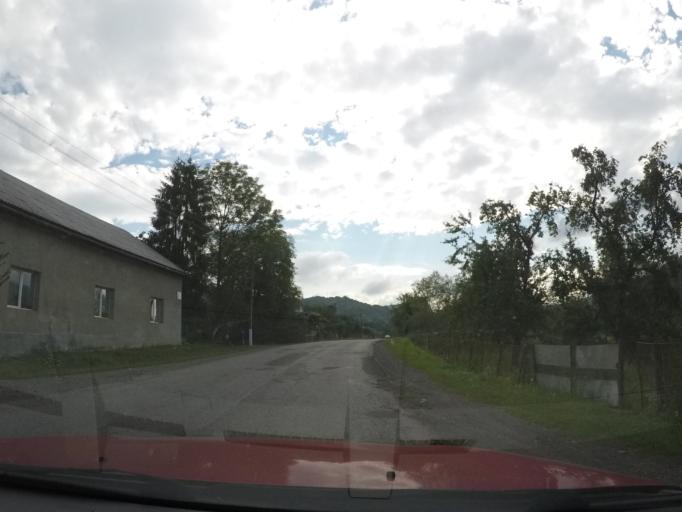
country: UA
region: Zakarpattia
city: Velykyi Bereznyi
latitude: 48.9531
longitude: 22.5187
